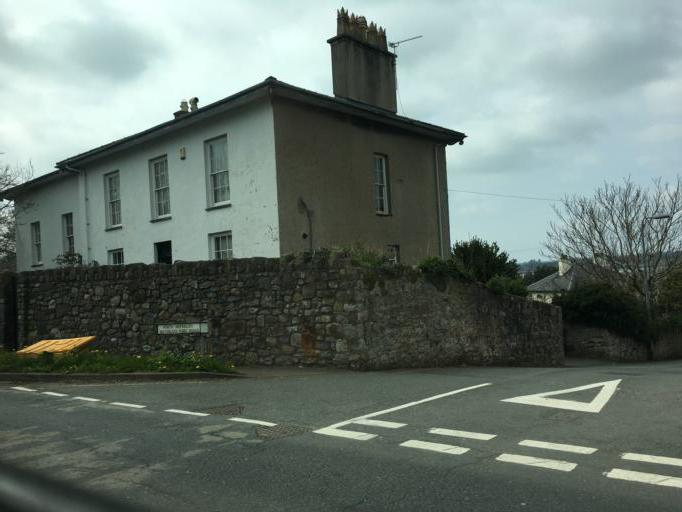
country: GB
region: Wales
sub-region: Gwynedd
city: Caernarfon
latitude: 53.1516
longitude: -4.2627
